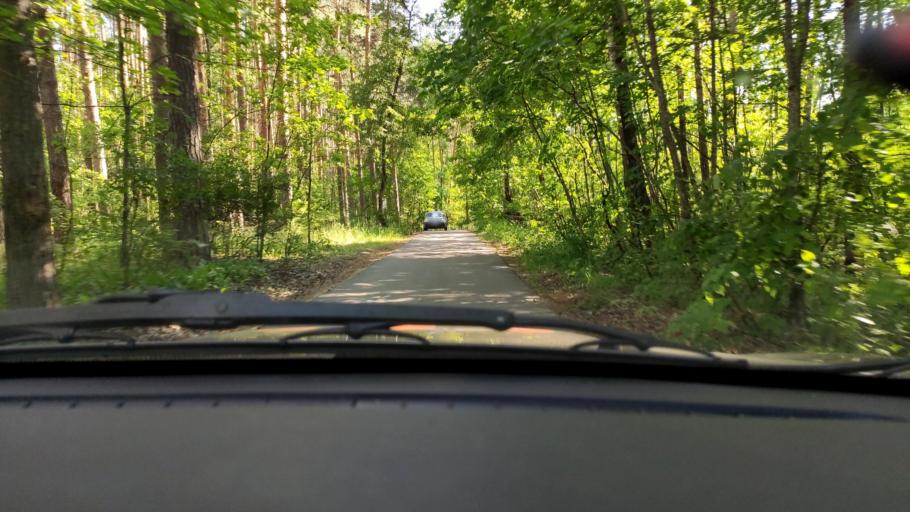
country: RU
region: Voronezj
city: Somovo
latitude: 51.8064
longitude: 39.3824
